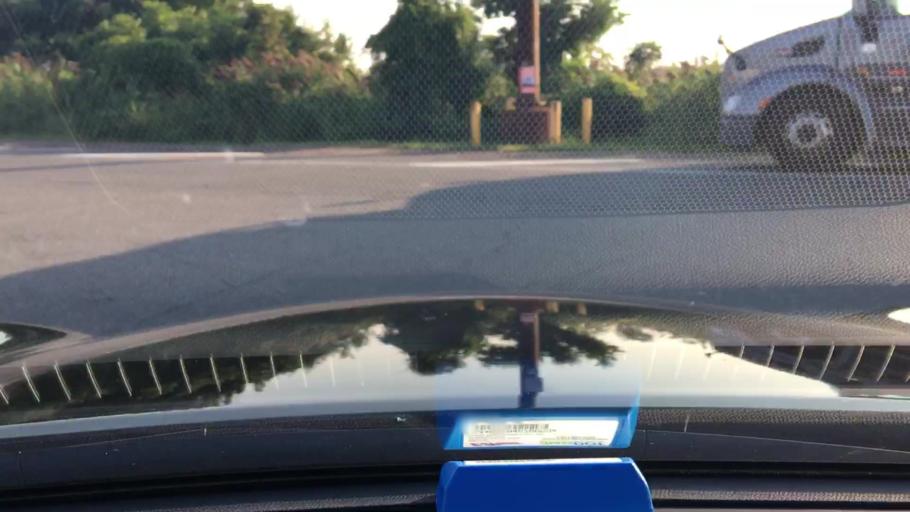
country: US
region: New Jersey
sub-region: Bergen County
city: Moonachie
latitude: 40.8223
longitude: -74.0307
